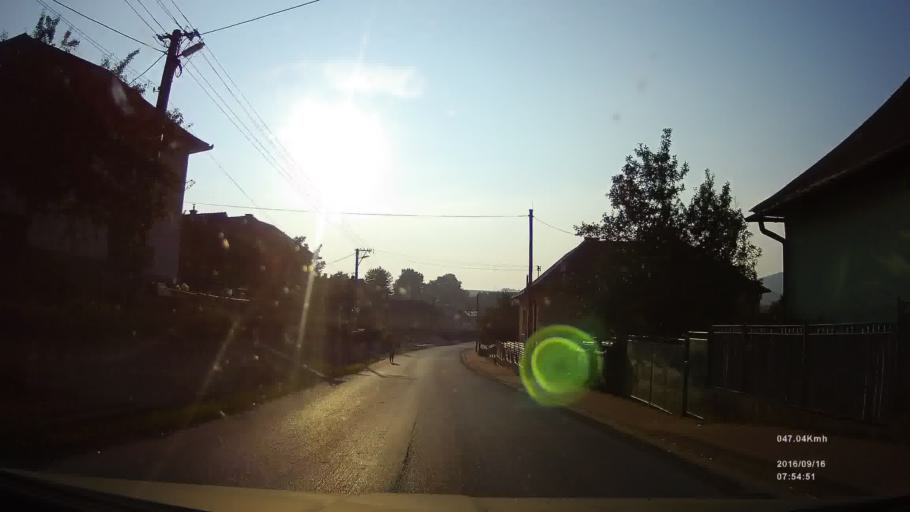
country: SK
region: Presovsky
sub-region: Okres Presov
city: Presov
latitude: 48.9168
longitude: 21.1205
